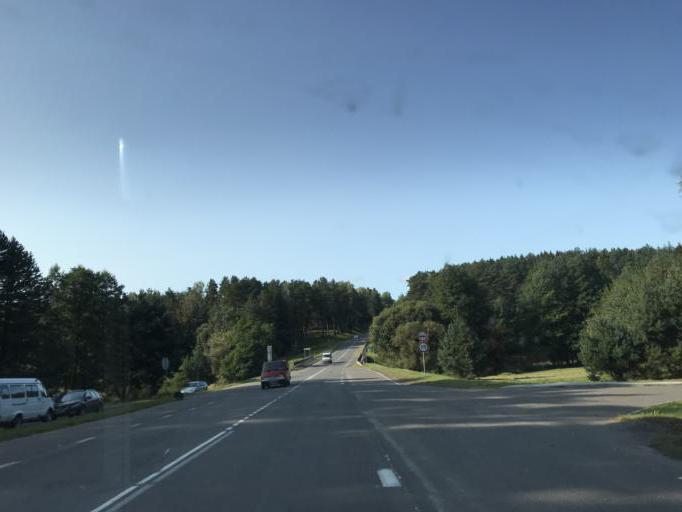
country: BY
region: Mogilev
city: Buynichy
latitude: 53.8140
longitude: 30.2344
